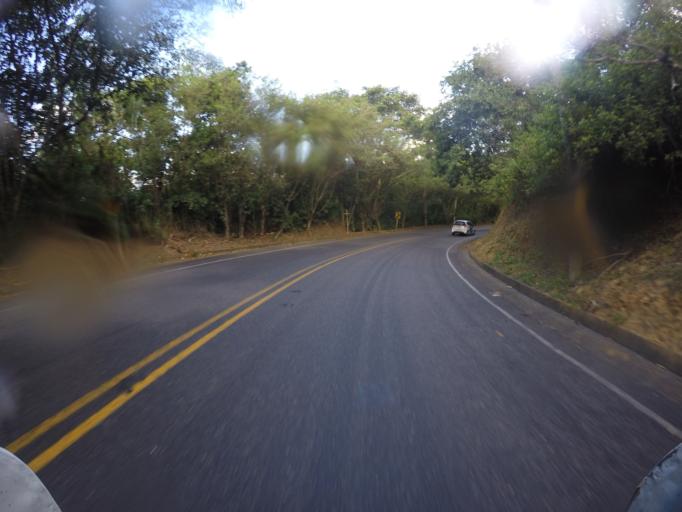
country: CO
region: Valle del Cauca
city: Cartago
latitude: 4.7297
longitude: -75.8687
